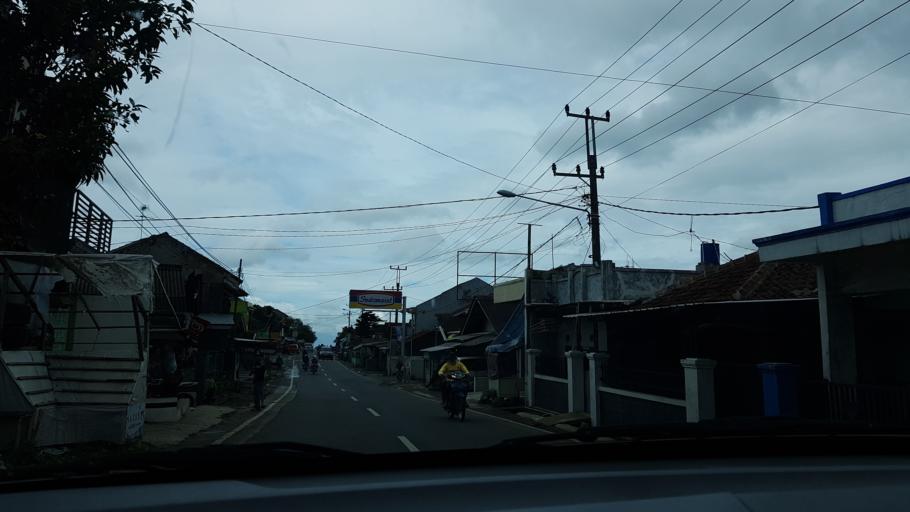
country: ID
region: West Java
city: Banjar
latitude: -7.1264
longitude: 107.4208
